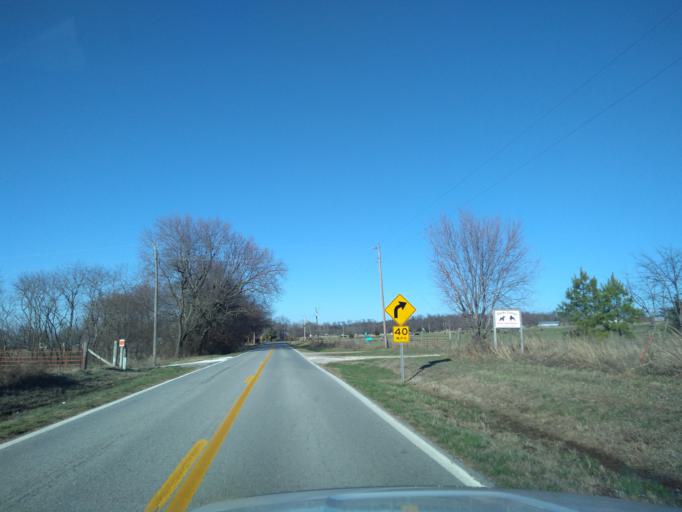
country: US
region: Arkansas
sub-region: Washington County
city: Lincoln
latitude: 35.9325
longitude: -94.3838
